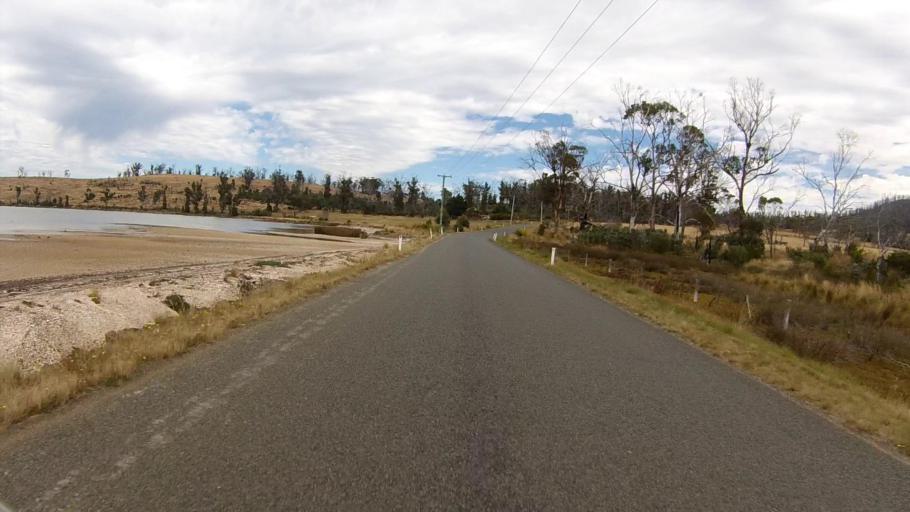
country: AU
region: Tasmania
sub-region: Sorell
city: Sorell
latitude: -42.8917
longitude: 147.7959
